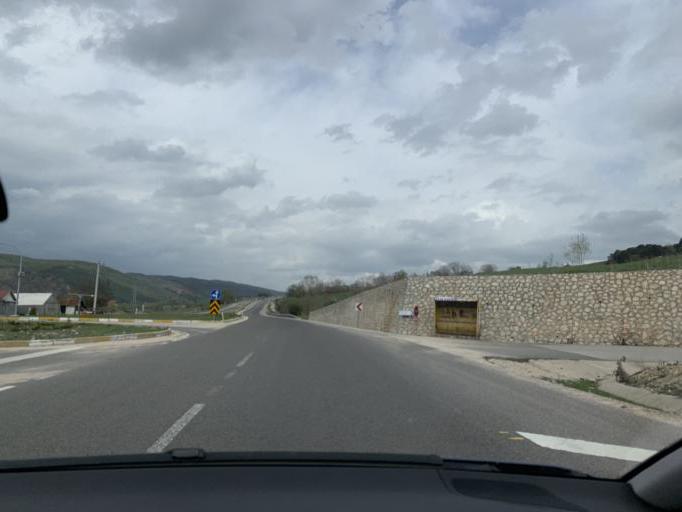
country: TR
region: Bolu
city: Gerede
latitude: 40.7880
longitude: 32.1264
